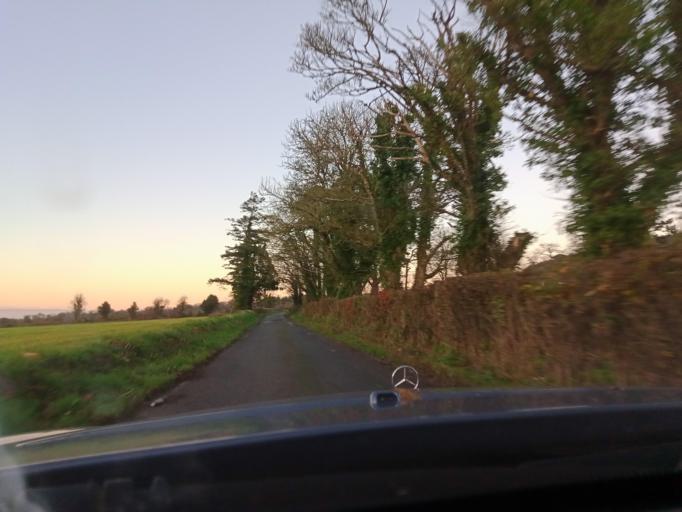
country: IE
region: Leinster
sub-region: Kilkenny
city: Thomastown
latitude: 52.4427
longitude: -7.1065
